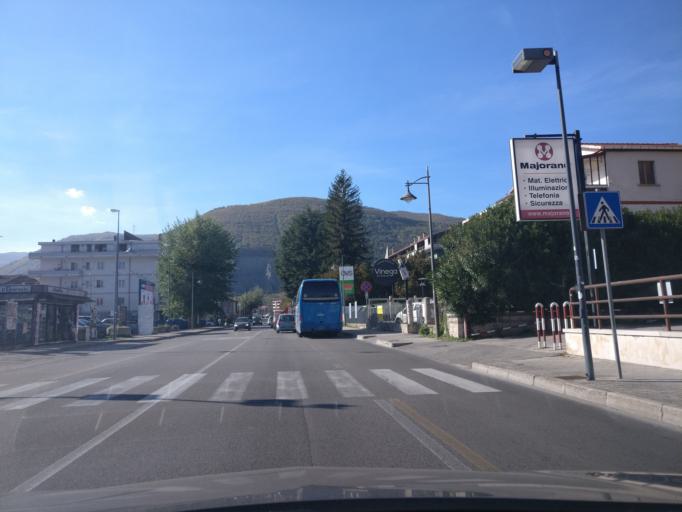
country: IT
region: Campania
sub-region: Provincia di Avellino
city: Torelli-Torrette
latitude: 40.9072
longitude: 14.7526
